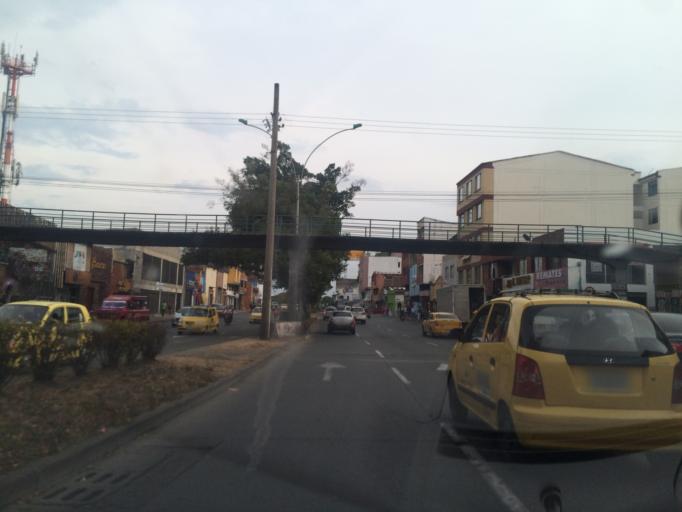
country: CO
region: Valle del Cauca
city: Cali
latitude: 3.4448
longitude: -76.5366
